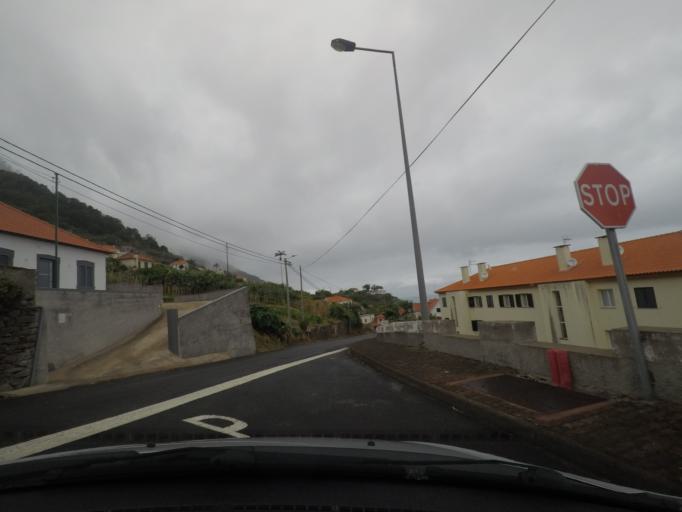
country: PT
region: Madeira
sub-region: Santana
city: Santana
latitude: 32.7883
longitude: -16.8551
